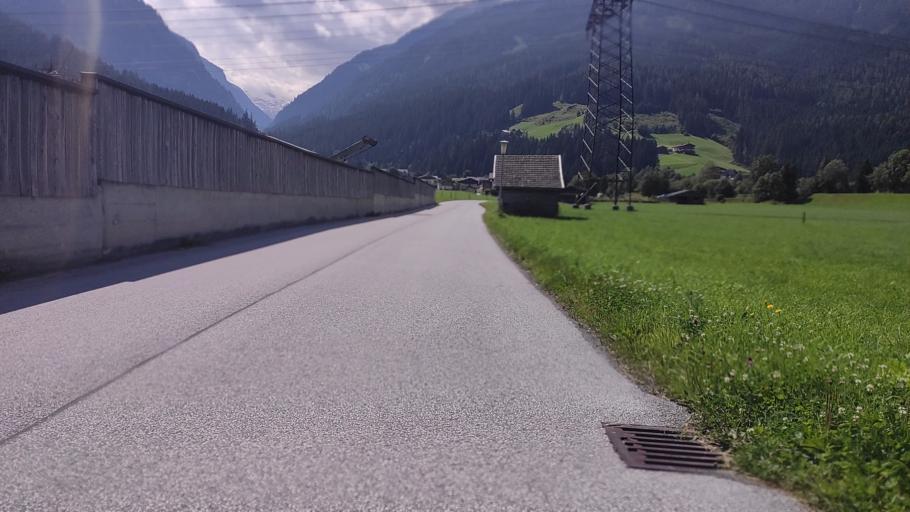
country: AT
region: Salzburg
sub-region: Politischer Bezirk Zell am See
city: Bramberg am Wildkogel
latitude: 47.2549
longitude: 12.3164
